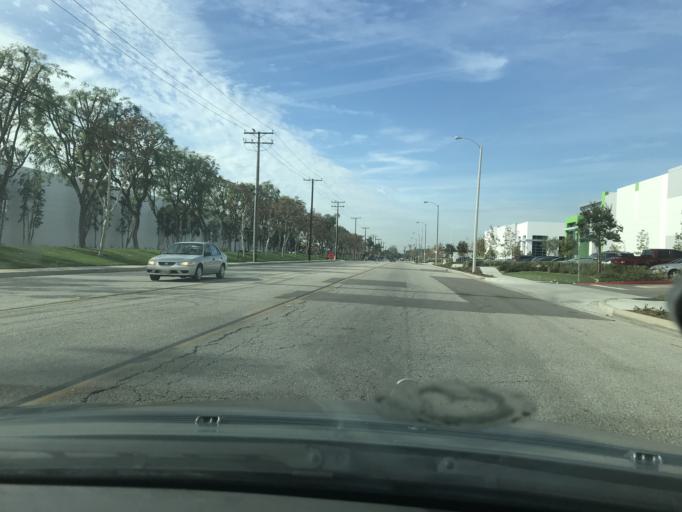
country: US
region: California
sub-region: Los Angeles County
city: Santa Fe Springs
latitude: 33.9318
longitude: -118.0670
